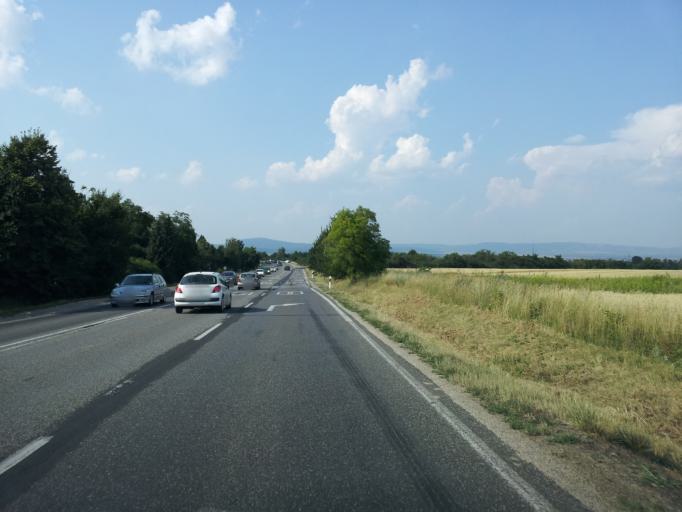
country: HU
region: Veszprem
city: Veszprem
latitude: 47.0960
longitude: 17.9333
